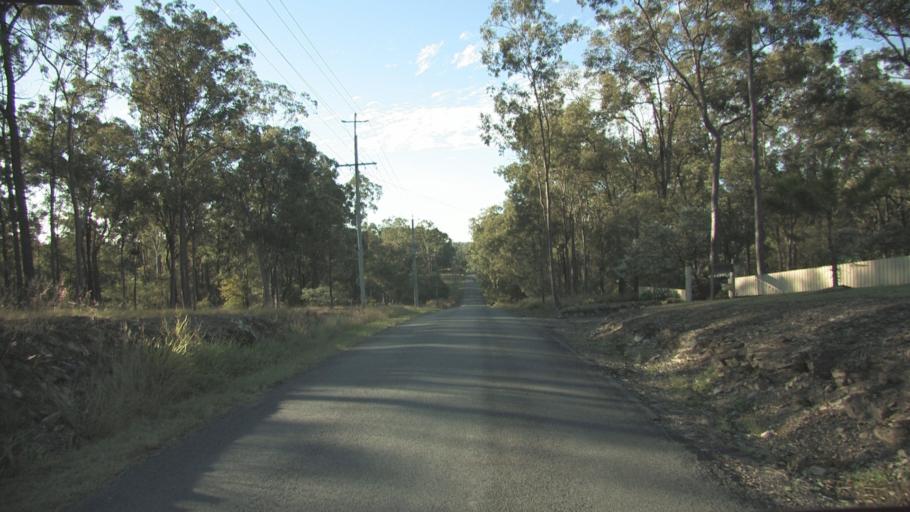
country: AU
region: Queensland
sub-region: Logan
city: Waterford West
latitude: -27.7299
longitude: 153.1523
